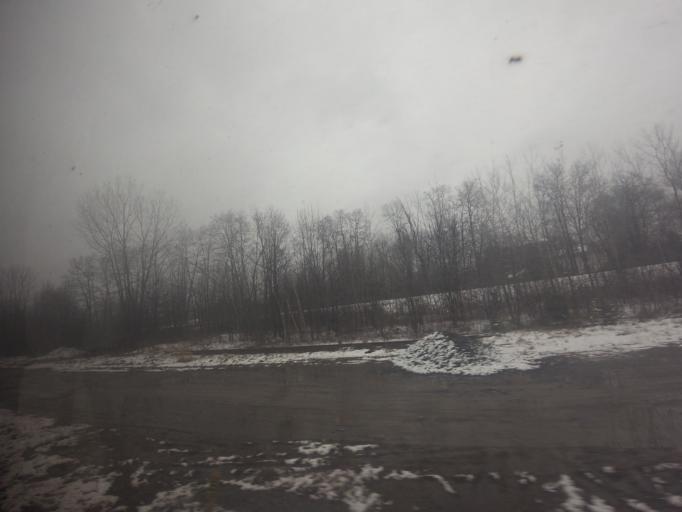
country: CA
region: Ontario
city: Cobourg
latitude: 43.9635
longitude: -78.1803
